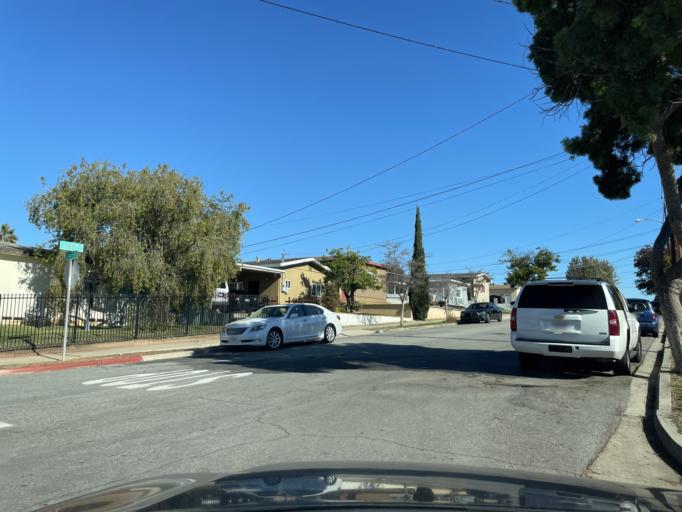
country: US
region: California
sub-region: San Diego County
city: National City
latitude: 32.6737
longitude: -117.0902
